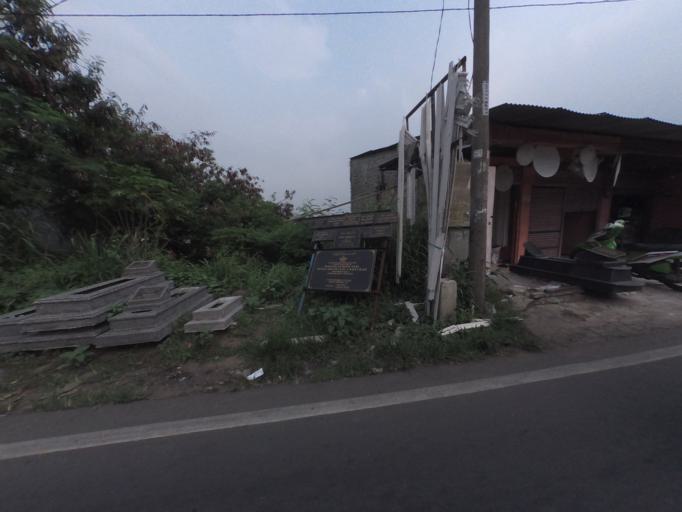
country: ID
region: West Java
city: Ciampea
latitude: -6.5578
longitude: 106.6924
